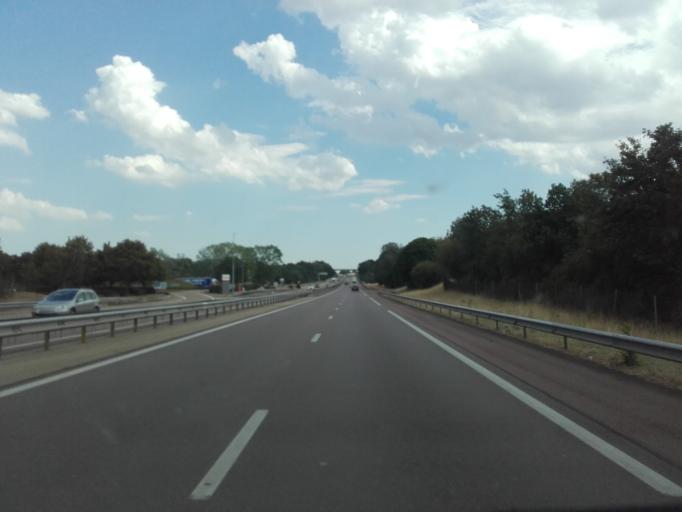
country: FR
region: Bourgogne
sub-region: Departement de la Cote-d'Or
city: Semur-en-Auxois
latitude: 47.4960
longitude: 4.1197
